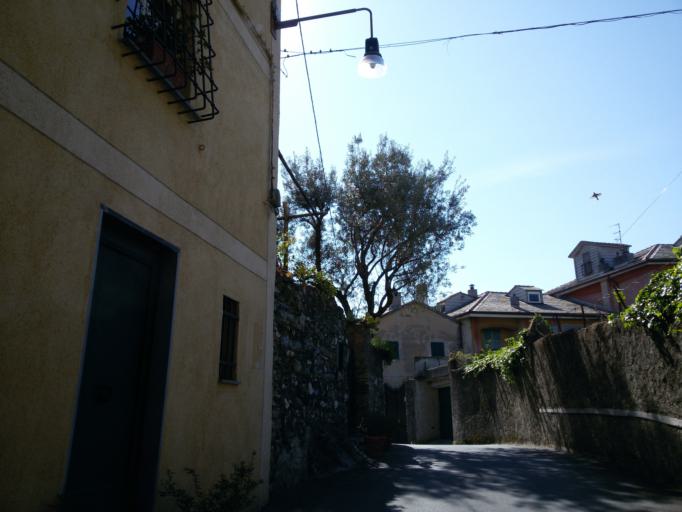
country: IT
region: Liguria
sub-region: Provincia di Genova
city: Bogliasco
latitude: 44.3903
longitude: 9.0110
